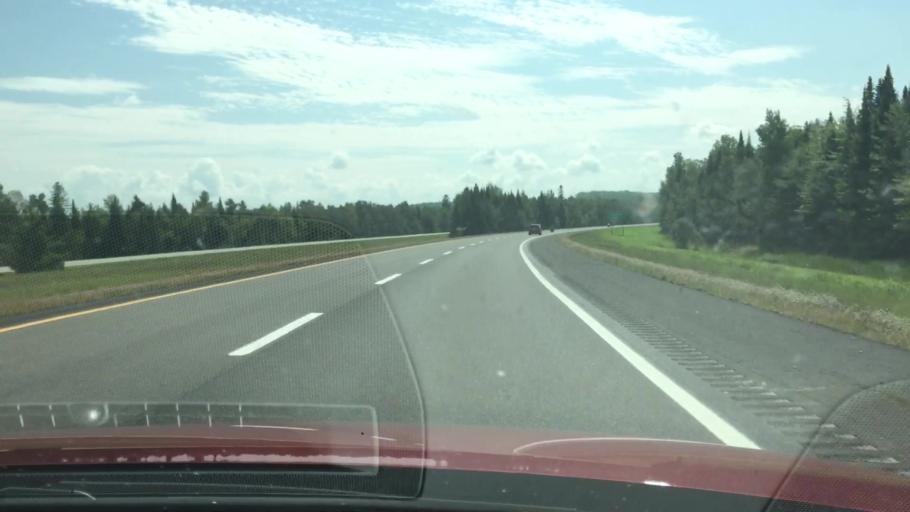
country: US
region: Maine
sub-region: Penobscot County
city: Patten
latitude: 45.9971
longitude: -68.2797
